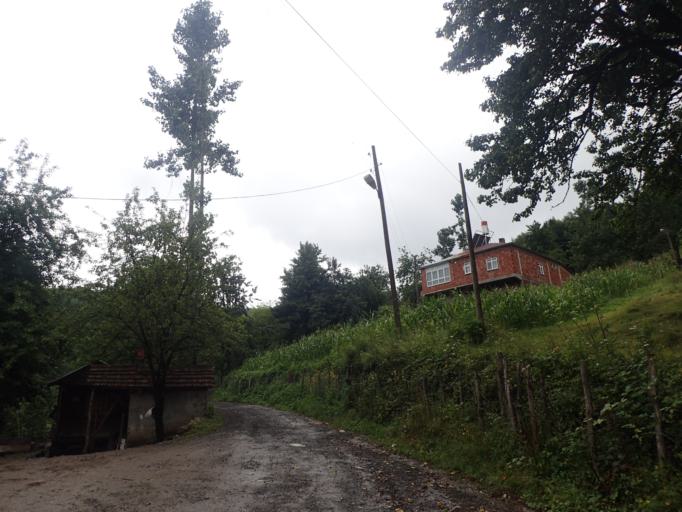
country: TR
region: Ordu
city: Akkus
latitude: 40.8063
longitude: 37.0994
